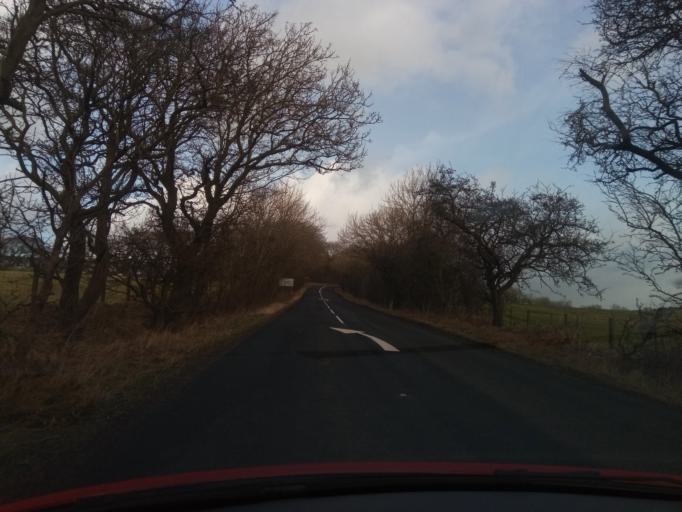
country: GB
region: England
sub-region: Northumberland
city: Acomb
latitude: 55.0982
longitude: -2.0469
